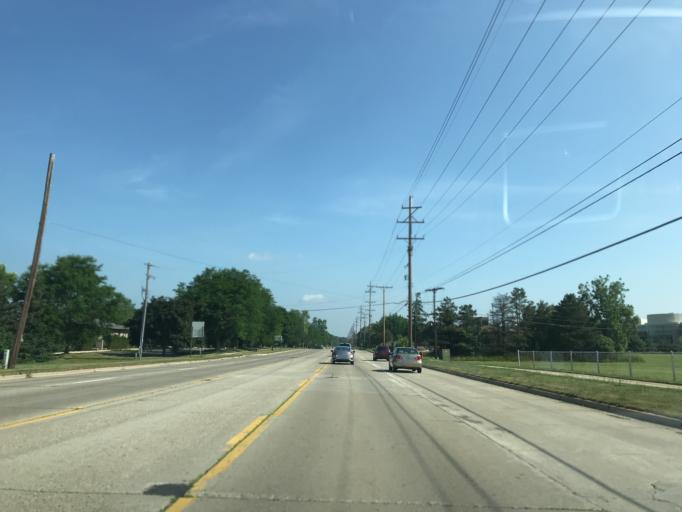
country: US
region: Michigan
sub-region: Ingham County
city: Okemos
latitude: 42.6984
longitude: -84.4323
